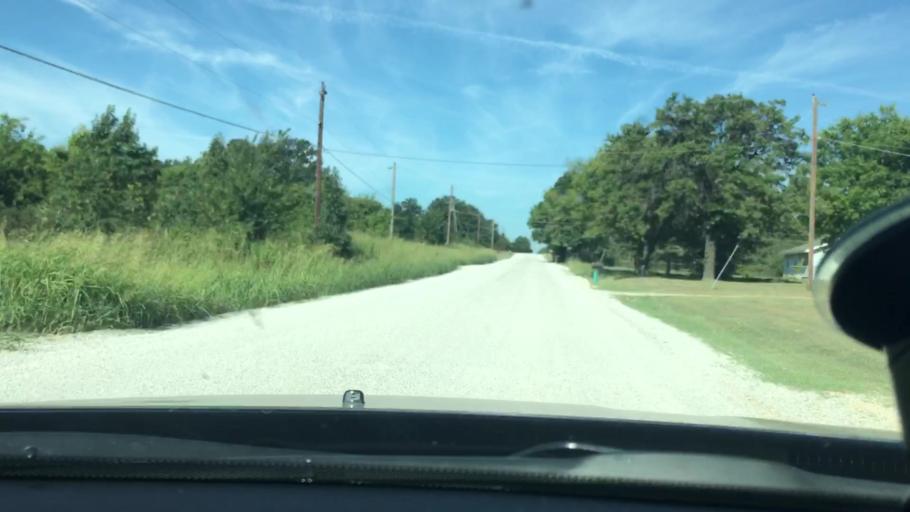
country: US
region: Oklahoma
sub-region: Carter County
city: Lone Grove
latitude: 34.2165
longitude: -97.2514
